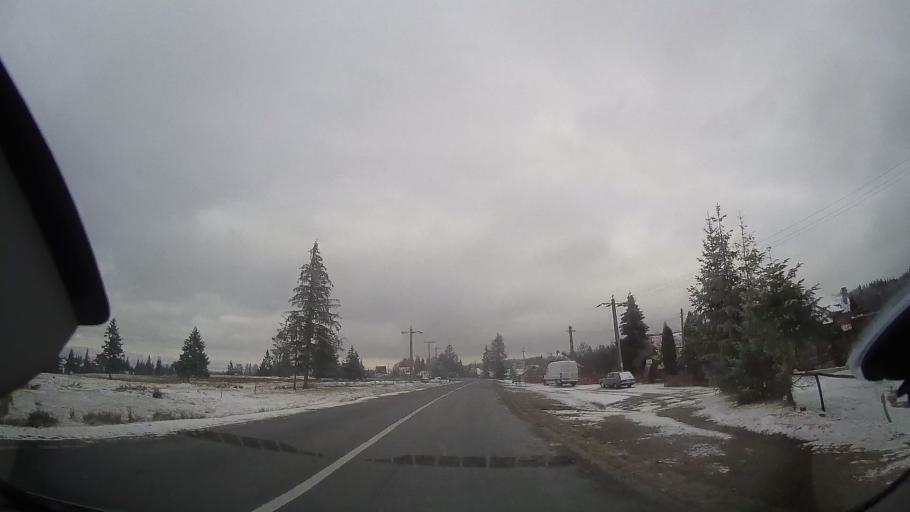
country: RO
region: Cluj
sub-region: Comuna Belis
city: Belis
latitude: 46.7018
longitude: 23.0365
